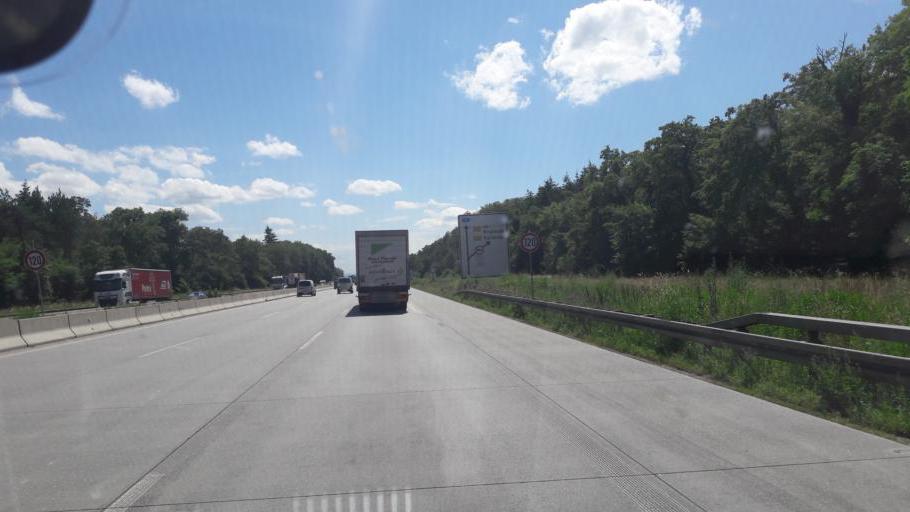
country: DE
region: Baden-Wuerttemberg
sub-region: Karlsruhe Region
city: Forst
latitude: 49.1571
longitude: 8.5657
